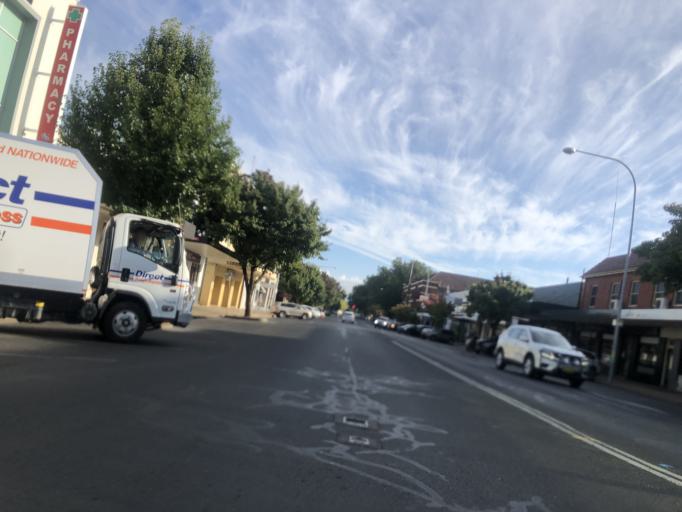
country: AU
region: New South Wales
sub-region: Orange Municipality
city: Orange
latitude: -33.2856
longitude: 149.1008
